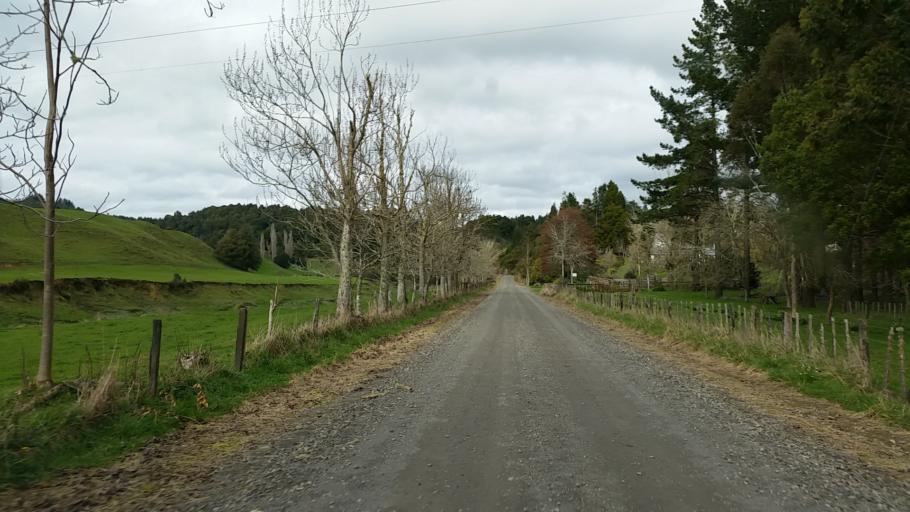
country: NZ
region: Taranaki
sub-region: New Plymouth District
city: Waitara
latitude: -39.1541
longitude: 174.5239
